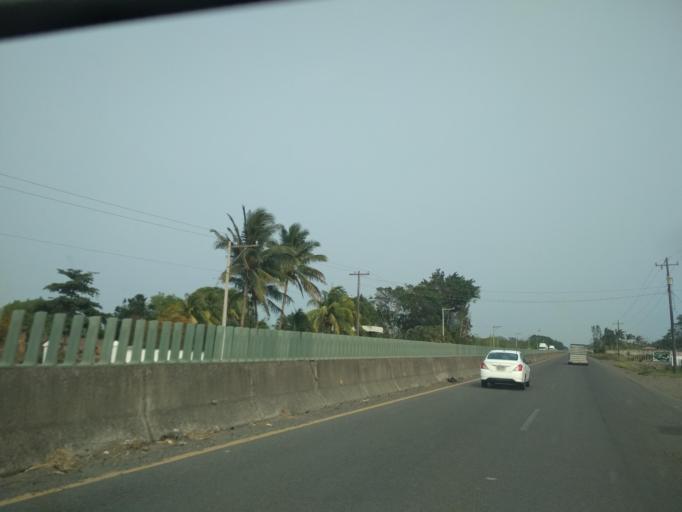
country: MX
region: Veracruz
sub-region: Veracruz
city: Hacienda Sotavento
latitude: 19.0955
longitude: -96.2100
